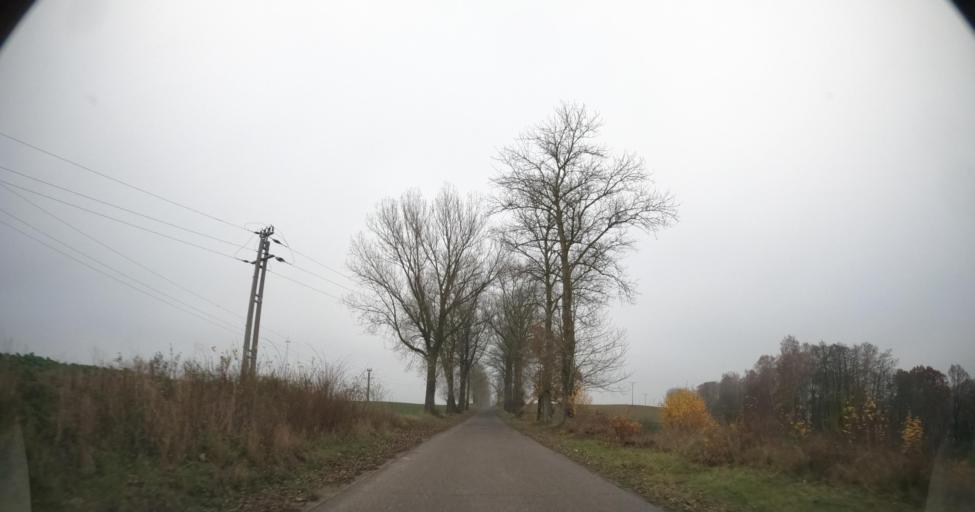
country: PL
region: West Pomeranian Voivodeship
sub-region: Powiat lobeski
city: Wegorzyno
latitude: 53.5435
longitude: 15.6237
